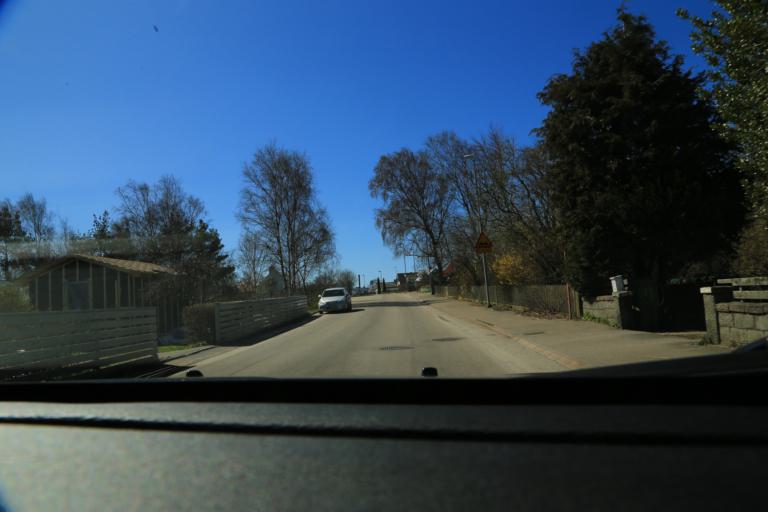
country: SE
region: Halland
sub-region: Varbergs Kommun
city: Varberg
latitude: 57.1042
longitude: 12.2885
